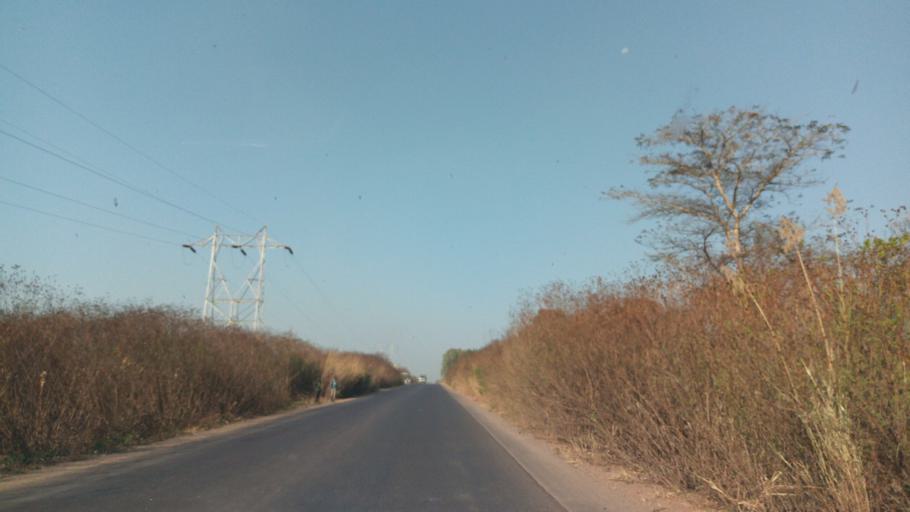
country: CD
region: Katanga
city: Likasi
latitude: -11.0028
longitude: 26.8488
